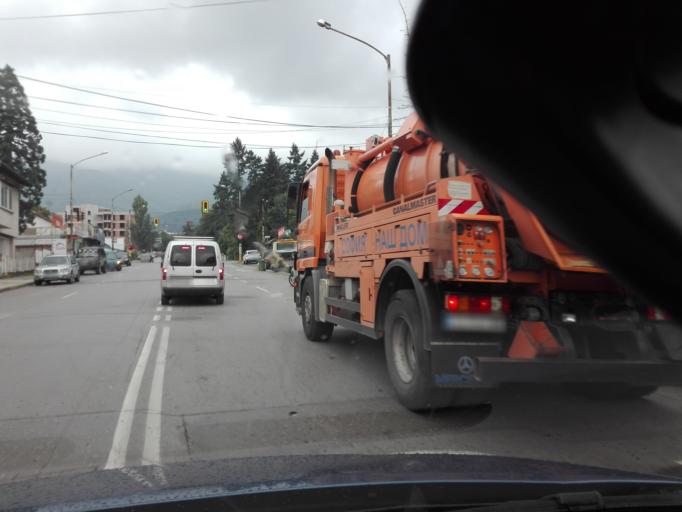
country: BG
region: Sofia-Capital
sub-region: Stolichna Obshtina
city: Sofia
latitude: 42.6609
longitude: 23.2651
